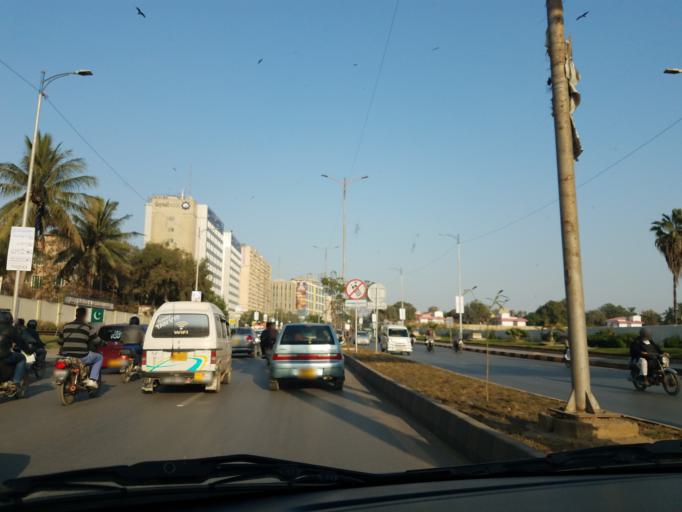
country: PK
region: Sindh
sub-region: Karachi District
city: Karachi
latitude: 24.8559
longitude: 67.0402
